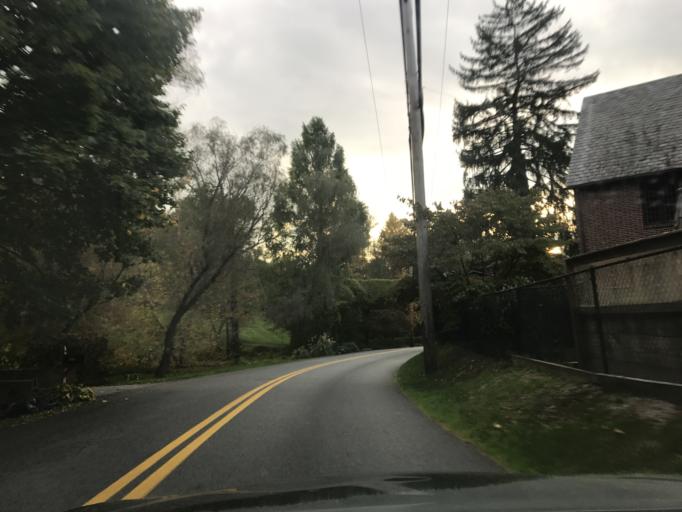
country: US
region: Maryland
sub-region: Baltimore County
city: Lutherville
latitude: 39.4022
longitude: -76.6408
